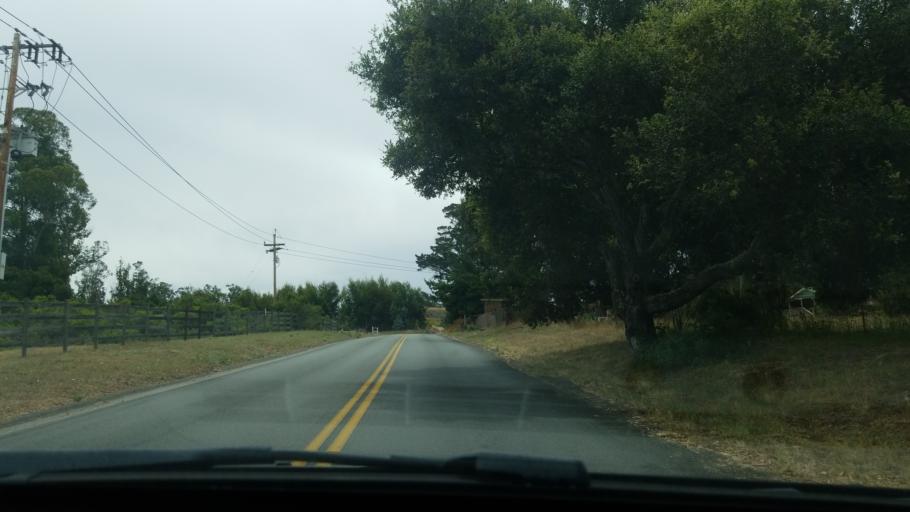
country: US
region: California
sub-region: San Luis Obispo County
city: Callender
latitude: 35.0739
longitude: -120.5412
